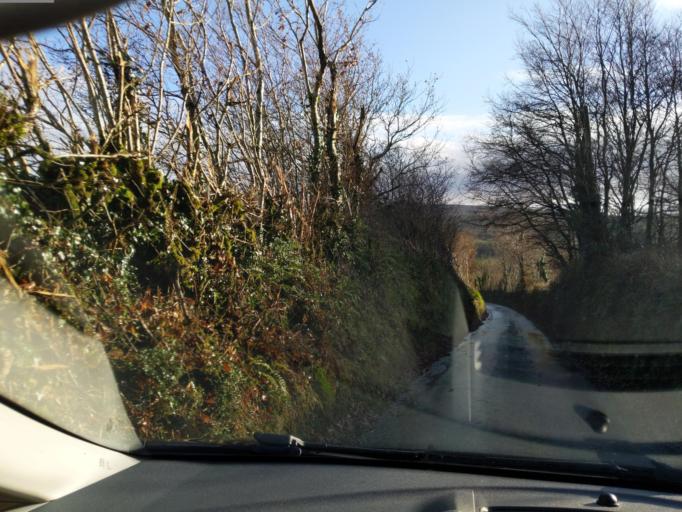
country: GB
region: England
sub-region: Devon
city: Okehampton
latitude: 50.7165
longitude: -4.0496
